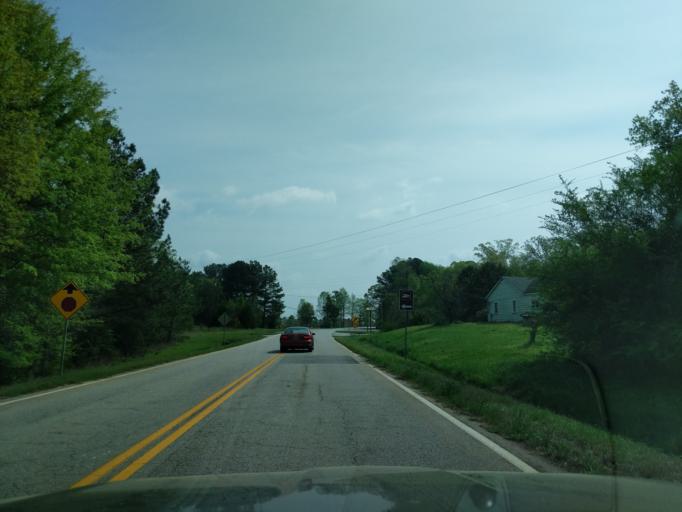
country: US
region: Georgia
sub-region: Lincoln County
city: Lincolnton
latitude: 33.8055
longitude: -82.3984
